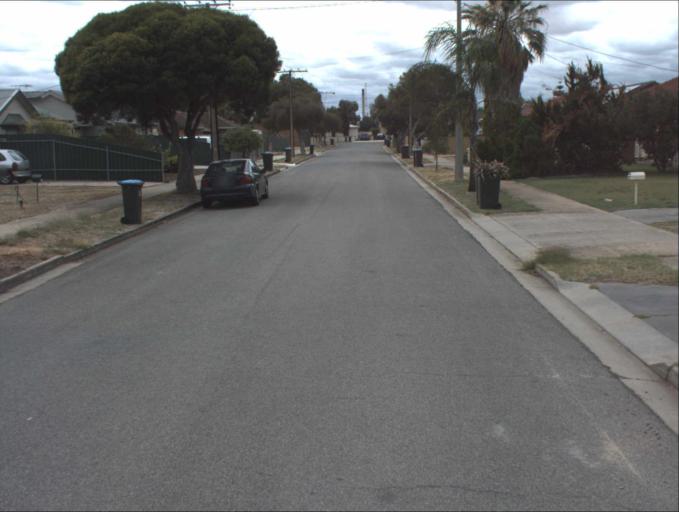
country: AU
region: South Australia
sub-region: Port Adelaide Enfield
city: Birkenhead
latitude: -34.8051
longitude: 138.4927
